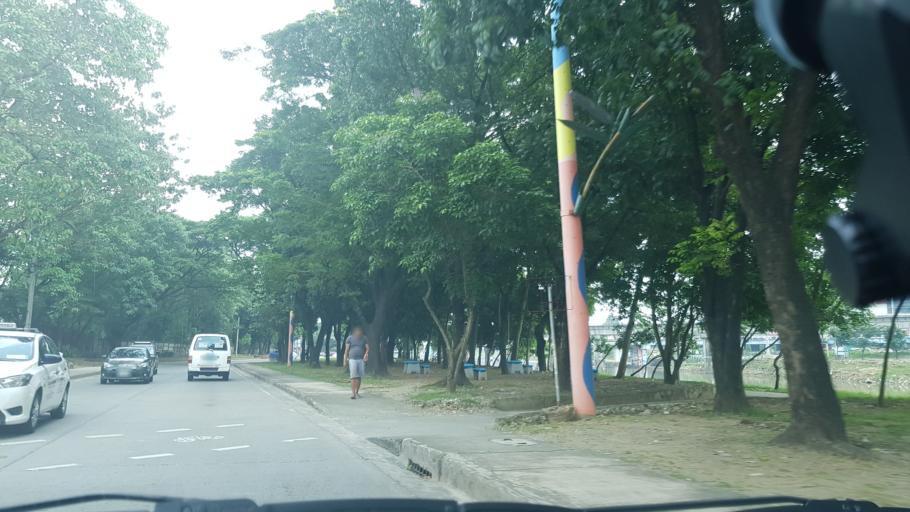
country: PH
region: Metro Manila
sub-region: Marikina
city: Calumpang
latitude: 14.6240
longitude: 121.0812
